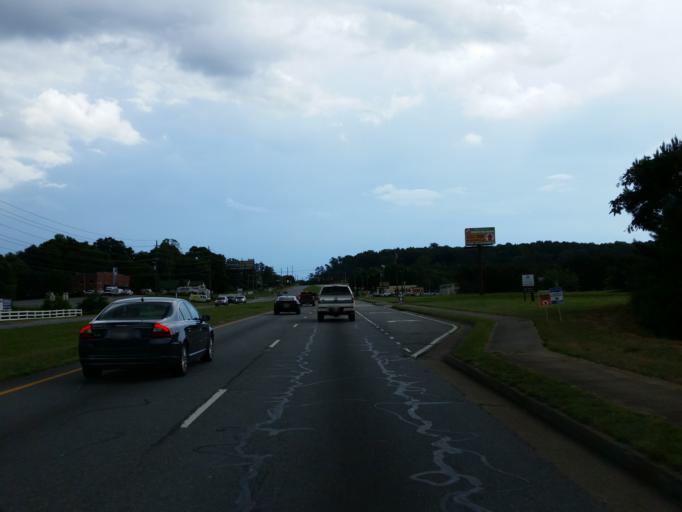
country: US
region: Georgia
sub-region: Cherokee County
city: Woodstock
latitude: 34.0864
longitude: -84.5066
